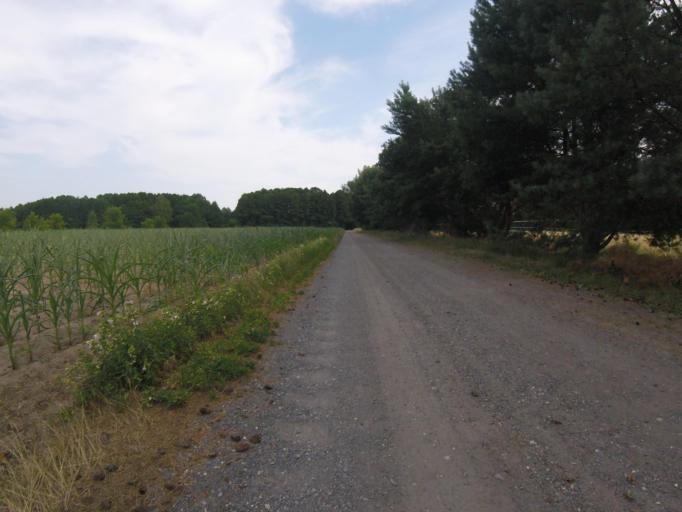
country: DE
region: Brandenburg
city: Erkner
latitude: 52.3112
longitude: 13.7542
